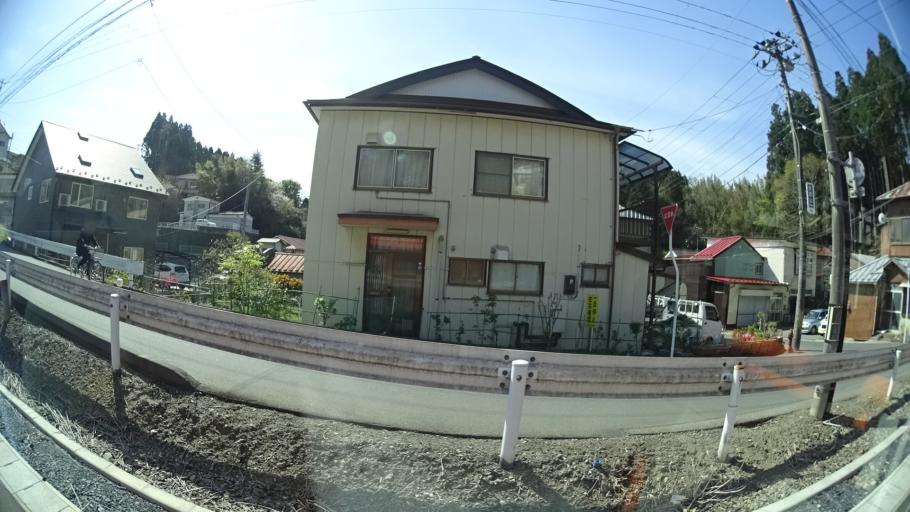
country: JP
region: Iwate
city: Ofunato
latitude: 38.9104
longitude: 141.5746
